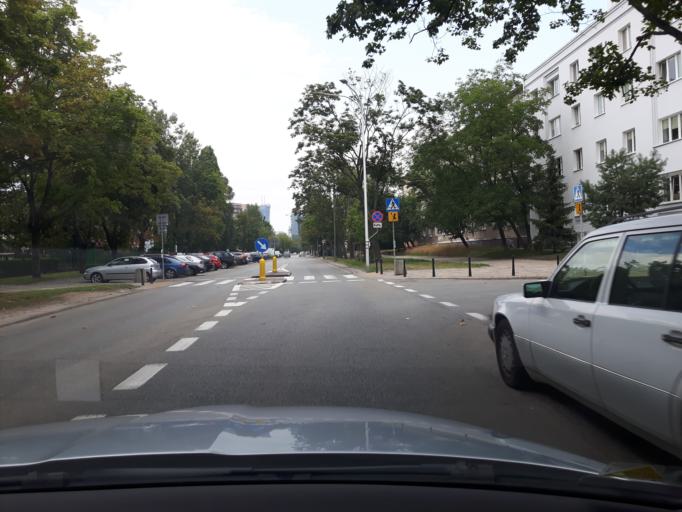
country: PL
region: Masovian Voivodeship
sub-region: Warszawa
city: Ochota
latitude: 52.2159
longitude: 20.9704
